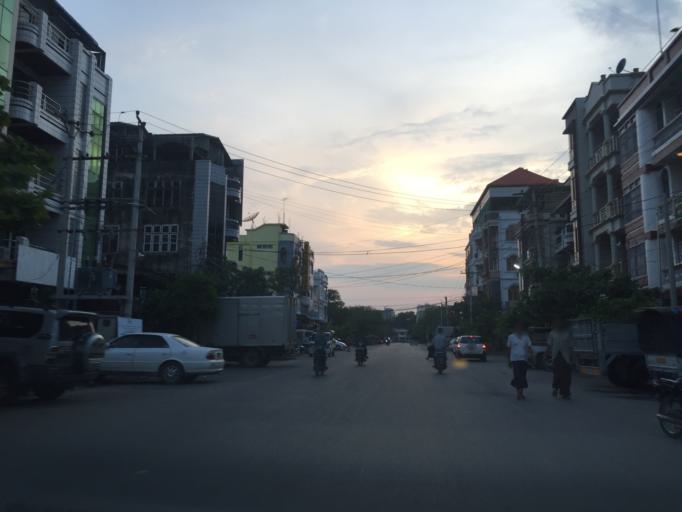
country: MM
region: Mandalay
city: Mandalay
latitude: 21.9799
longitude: 96.0899
